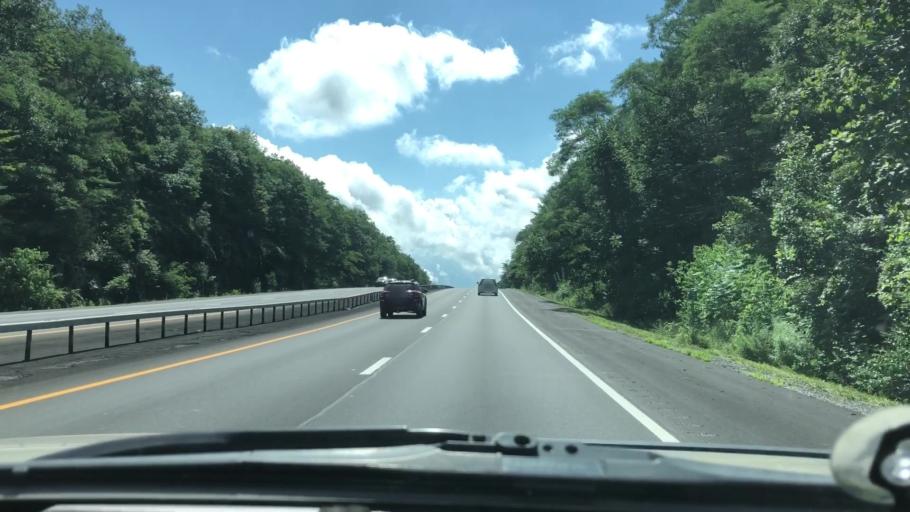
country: US
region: New York
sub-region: Greene County
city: Cairo
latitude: 42.3061
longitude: -74.0010
